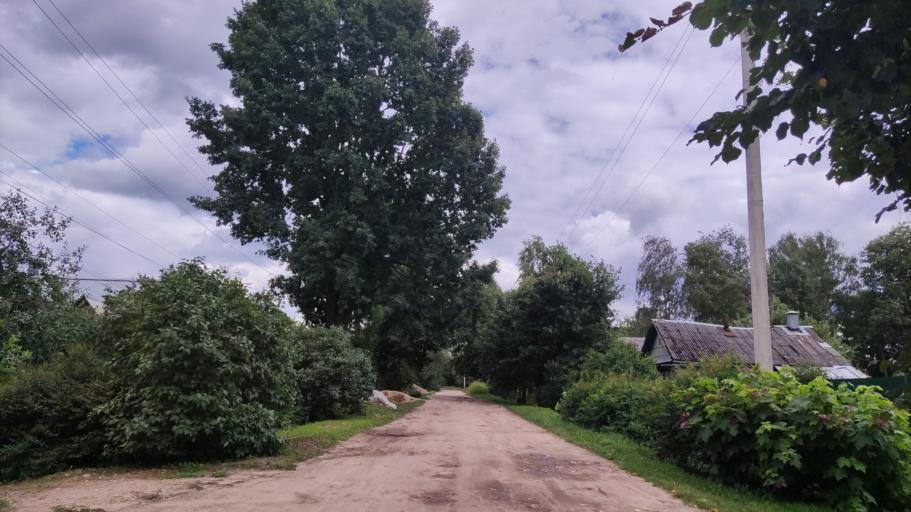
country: RU
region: Tverskaya
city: Rzhev
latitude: 56.2468
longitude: 34.3016
